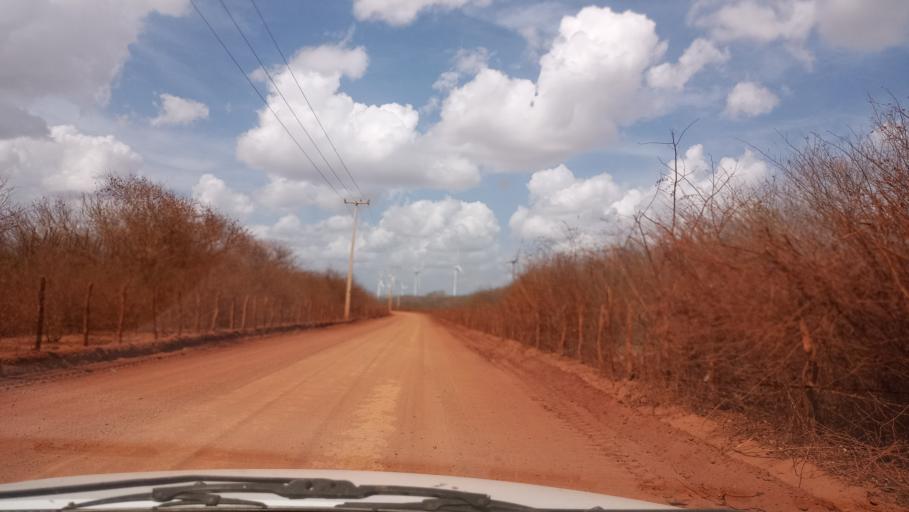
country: BR
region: Rio Grande do Norte
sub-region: Joao Camara
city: Joao Camara
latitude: -5.3639
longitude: -35.8368
